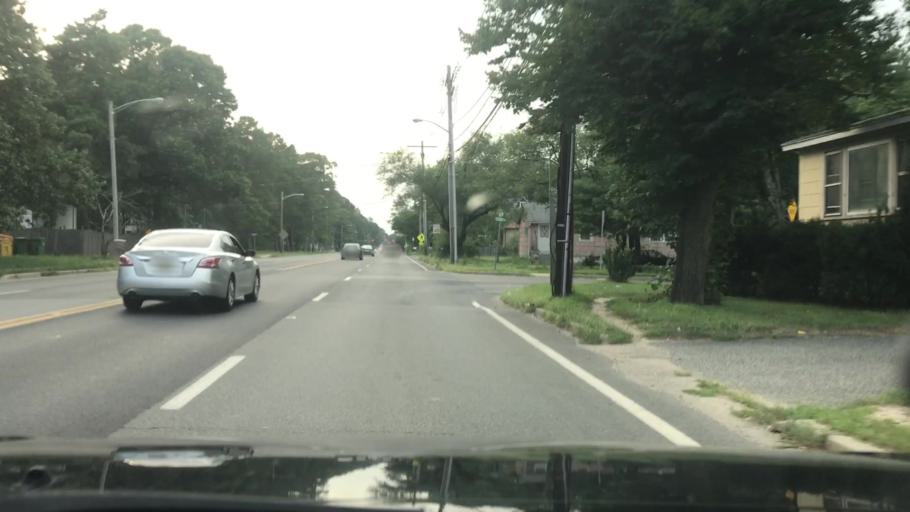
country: US
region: New Jersey
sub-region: Ocean County
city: Lakewood
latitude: 40.1077
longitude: -74.2325
